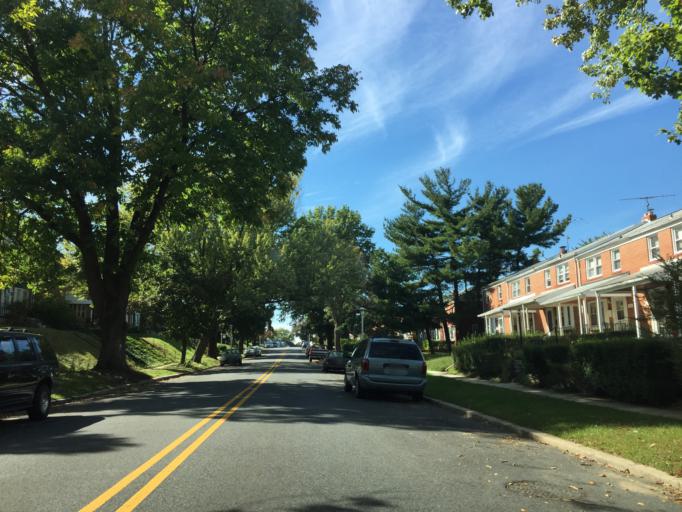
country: US
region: Maryland
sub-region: Baltimore County
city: Towson
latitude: 39.3712
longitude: -76.5918
